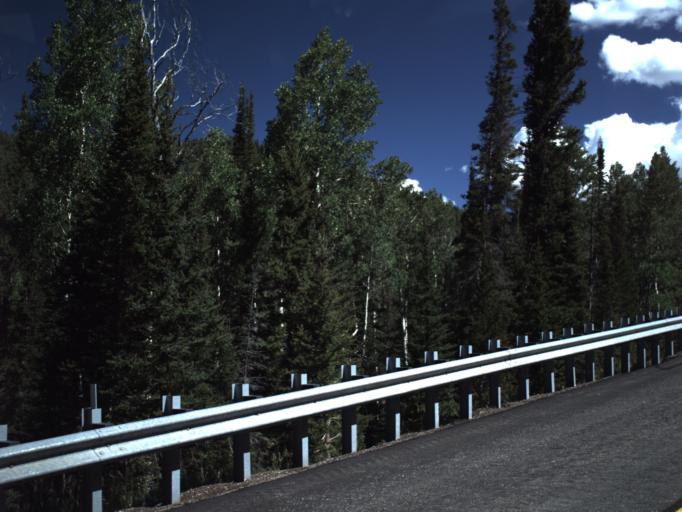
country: US
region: Utah
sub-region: Piute County
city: Junction
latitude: 38.3083
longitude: -112.4144
